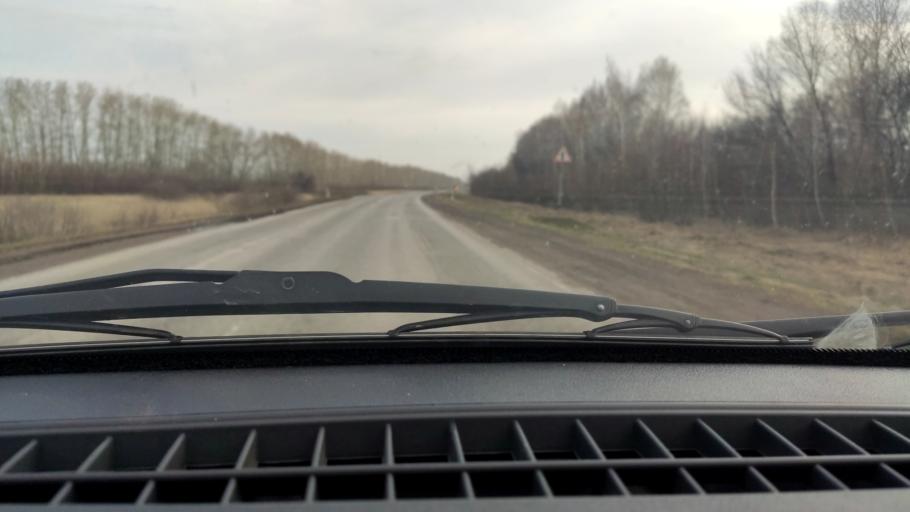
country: RU
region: Bashkortostan
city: Davlekanovo
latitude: 54.3489
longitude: 55.1777
